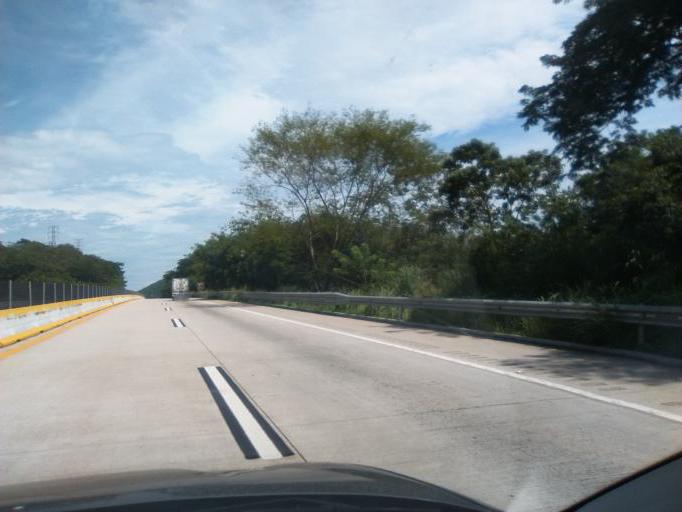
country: MX
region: Guerrero
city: Xaltianguis
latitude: 17.0033
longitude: -99.6750
